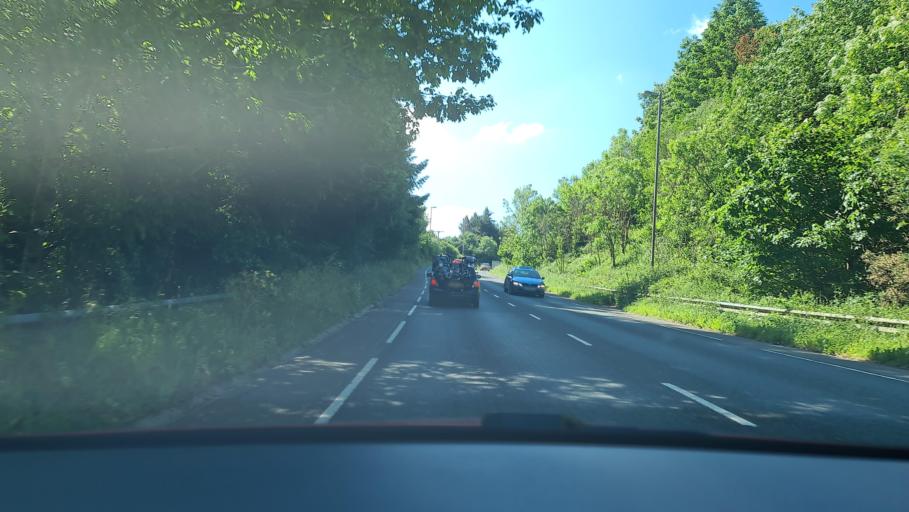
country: GB
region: England
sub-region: Cornwall
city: Liskeard
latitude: 50.4541
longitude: -4.4498
